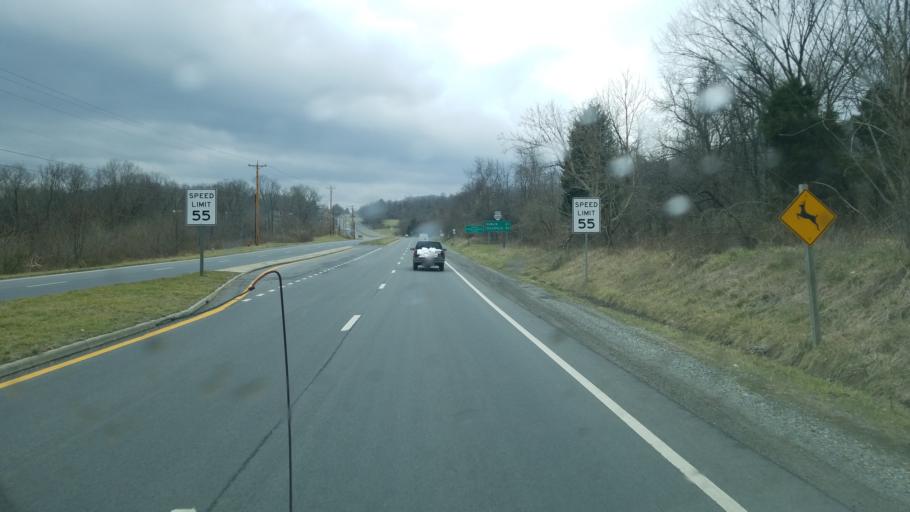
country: US
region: Virginia
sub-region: Giles County
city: Pearisburg
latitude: 37.3196
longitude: -80.7303
